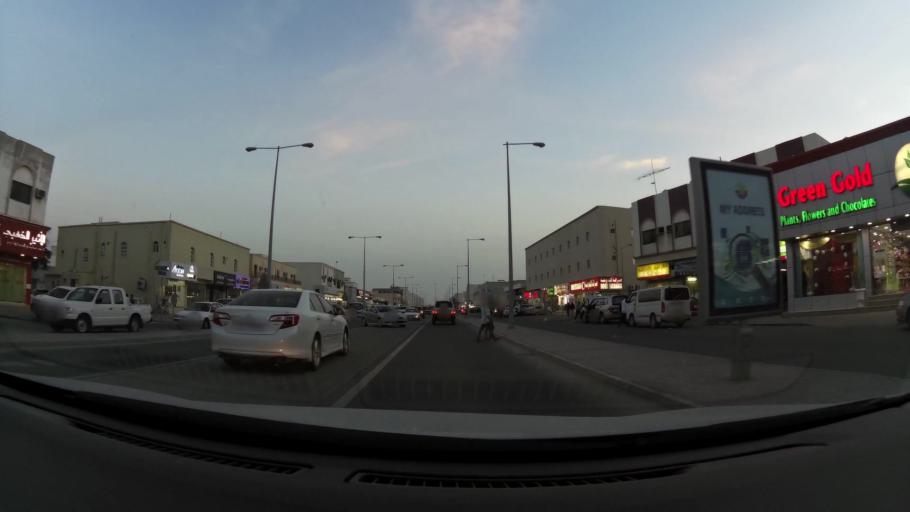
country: QA
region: Al Wakrah
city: Al Wakrah
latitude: 25.1551
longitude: 51.5992
